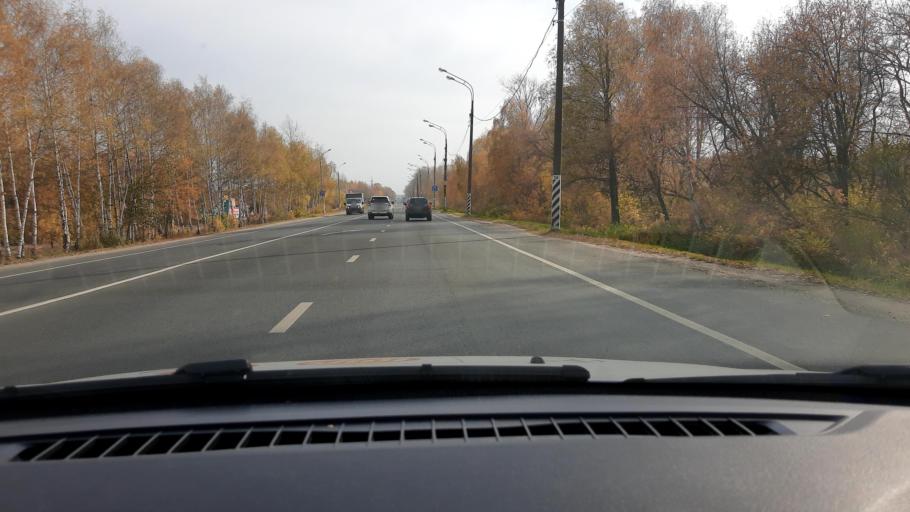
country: RU
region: Nizjnij Novgorod
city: Kstovo
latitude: 56.1449
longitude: 44.2189
